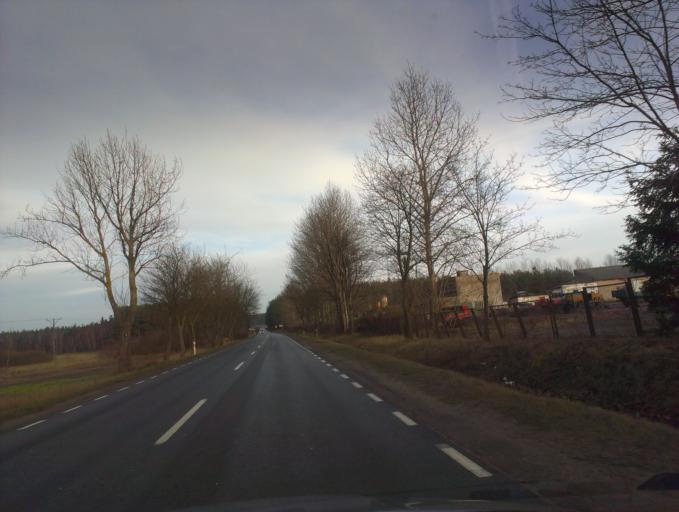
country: PL
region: West Pomeranian Voivodeship
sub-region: Powiat szczecinecki
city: Szczecinek
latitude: 53.7214
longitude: 16.7524
